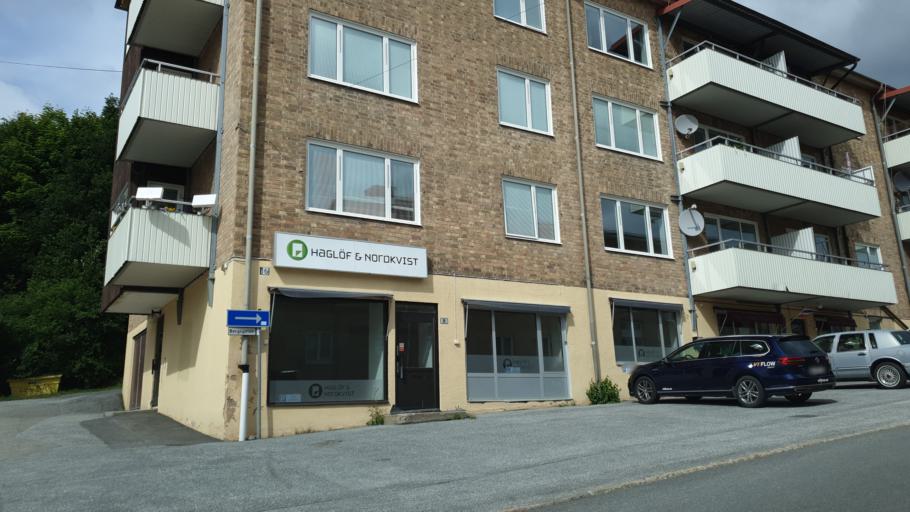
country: SE
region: Vaesternorrland
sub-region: OErnskoeldsviks Kommun
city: Ornskoldsvik
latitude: 63.2925
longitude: 18.7118
